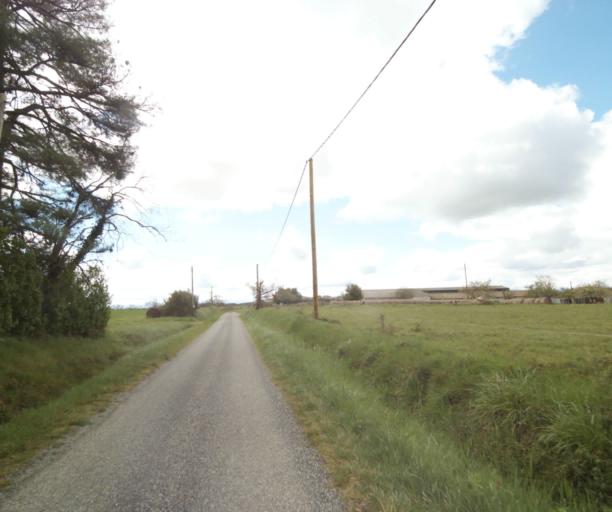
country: FR
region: Midi-Pyrenees
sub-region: Departement de l'Ariege
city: Saverdun
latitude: 43.2144
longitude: 1.5817
